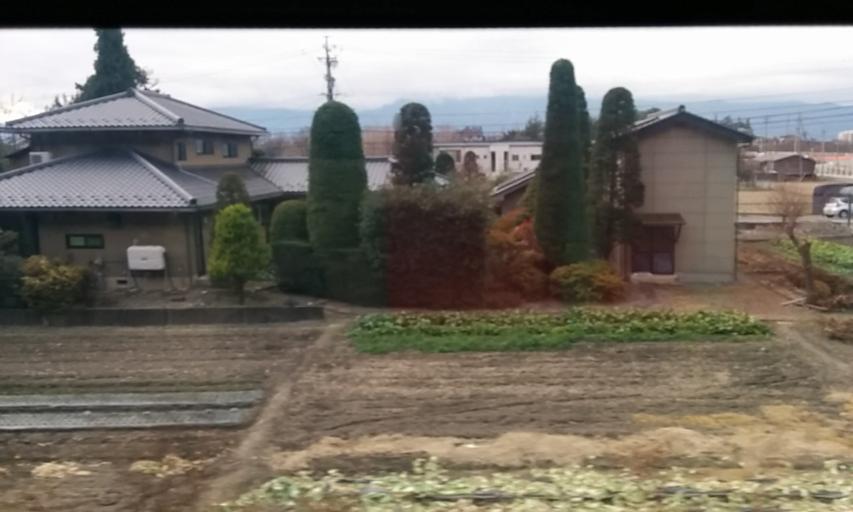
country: JP
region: Nagano
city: Matsumoto
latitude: 36.2640
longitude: 137.9481
